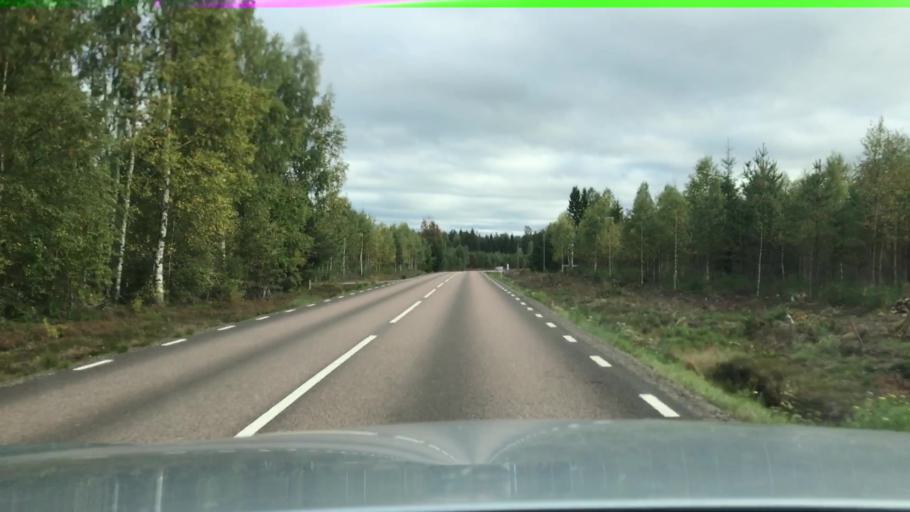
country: SE
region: Vaermland
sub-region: Forshaga Kommun
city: Forshaga
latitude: 59.5086
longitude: 13.4217
